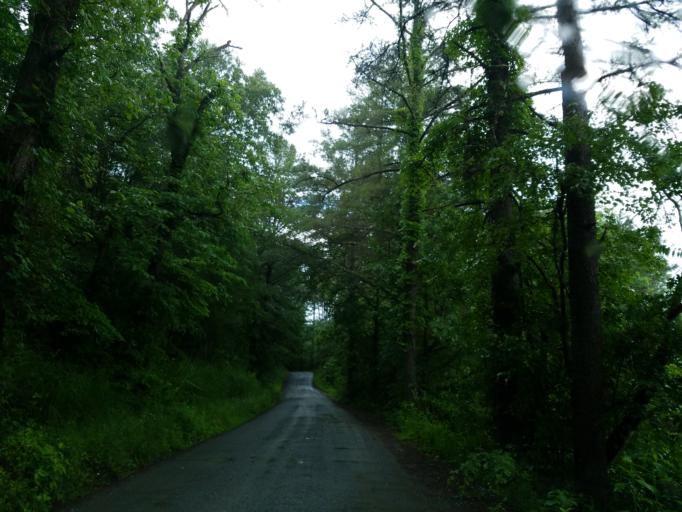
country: US
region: Georgia
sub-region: Fannin County
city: Blue Ridge
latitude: 34.7581
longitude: -84.1939
